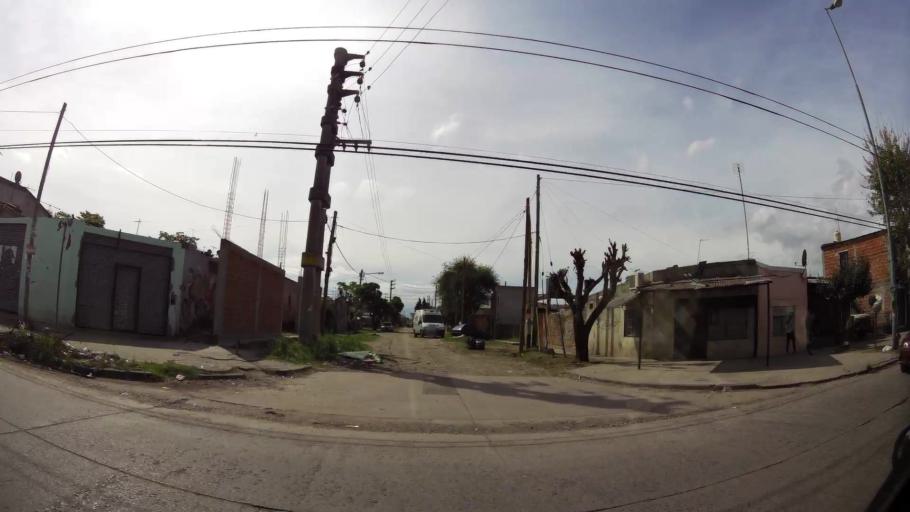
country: AR
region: Buenos Aires
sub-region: Partido de Quilmes
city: Quilmes
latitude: -34.7622
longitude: -58.2452
